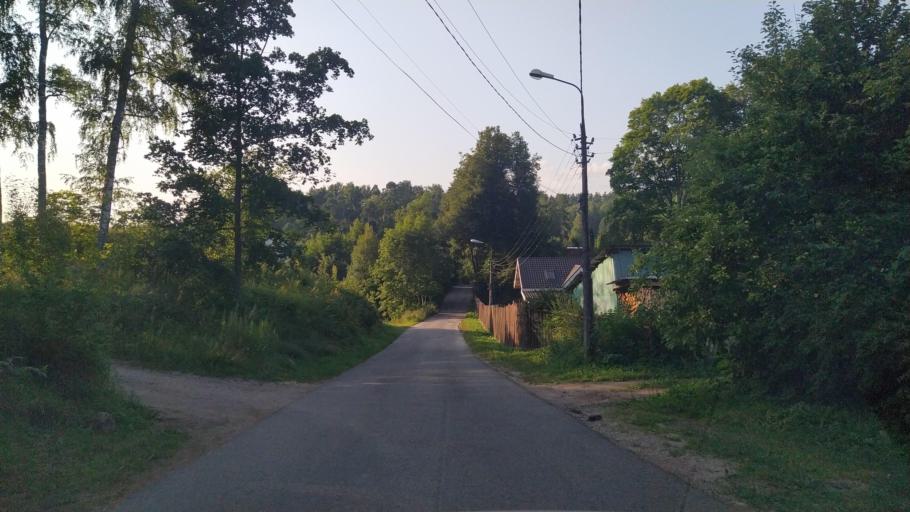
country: RU
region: Pskov
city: Pushkinskiye Gory
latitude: 57.0227
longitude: 28.9184
